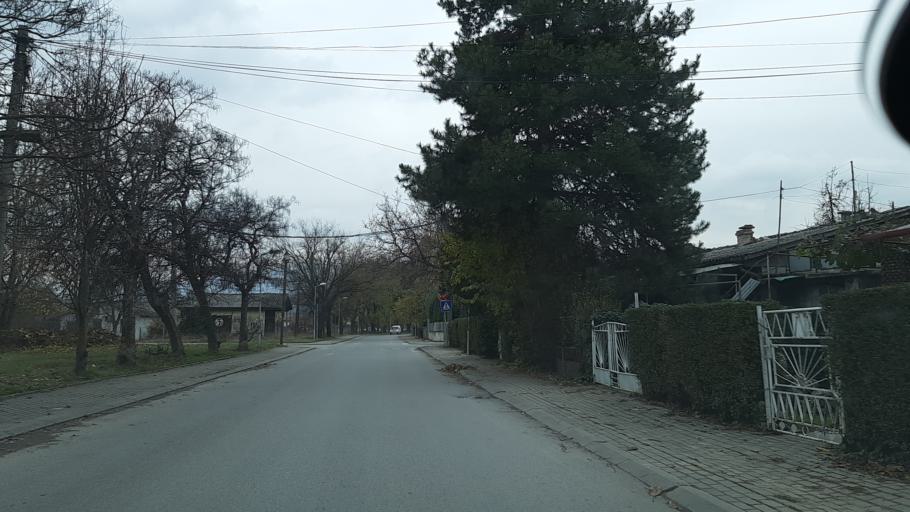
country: MK
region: Kisela Voda
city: Usje
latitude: 41.9734
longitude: 21.4779
